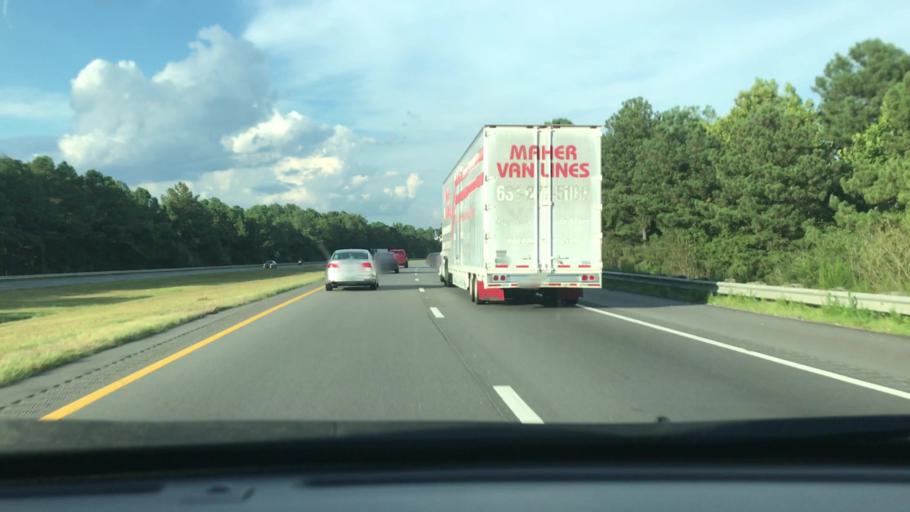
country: US
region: North Carolina
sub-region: Cumberland County
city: Hope Mills
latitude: 34.9322
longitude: -78.9367
